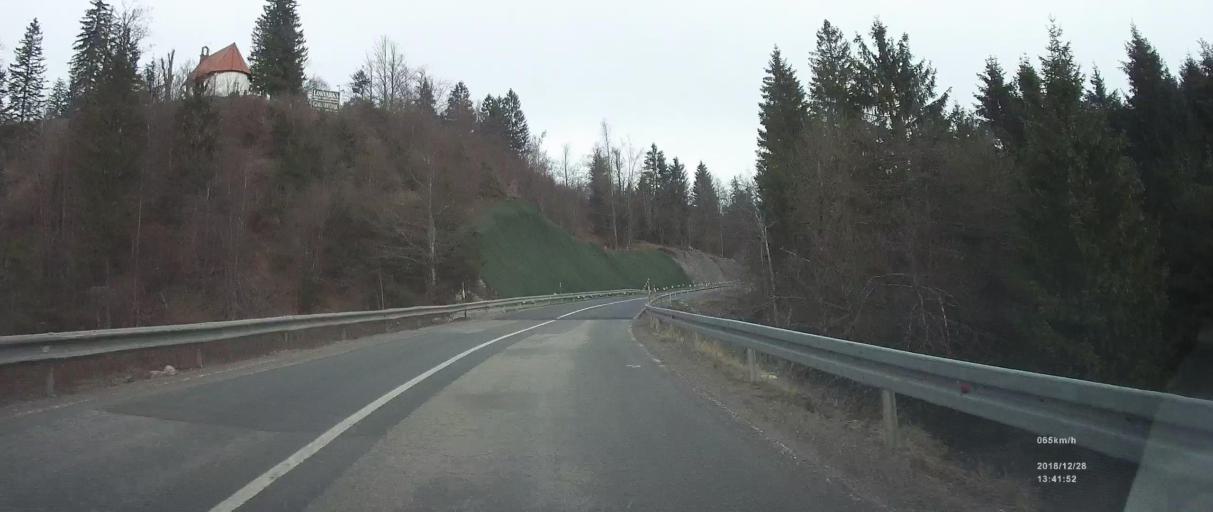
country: HR
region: Primorsko-Goranska
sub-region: Grad Delnice
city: Delnice
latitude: 45.3572
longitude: 14.7611
